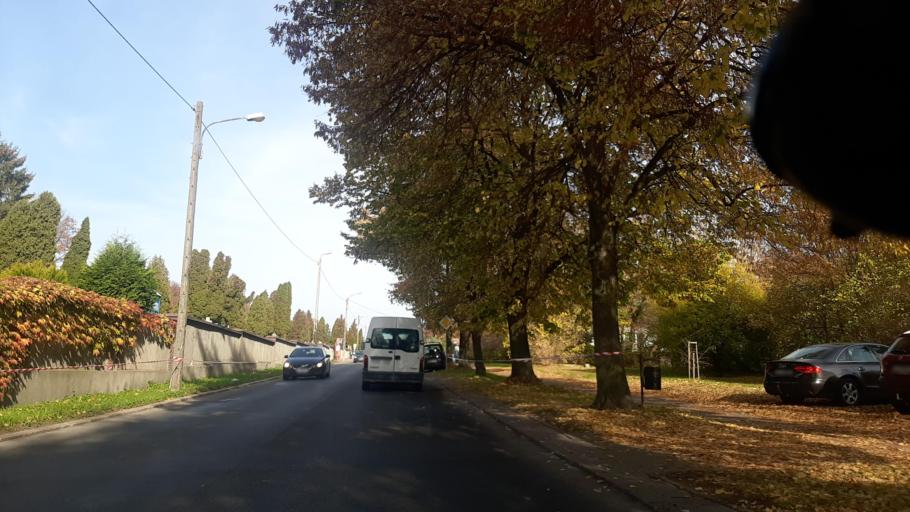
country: PL
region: Lublin Voivodeship
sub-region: Powiat lubelski
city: Lublin
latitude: 51.2625
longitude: 22.5806
